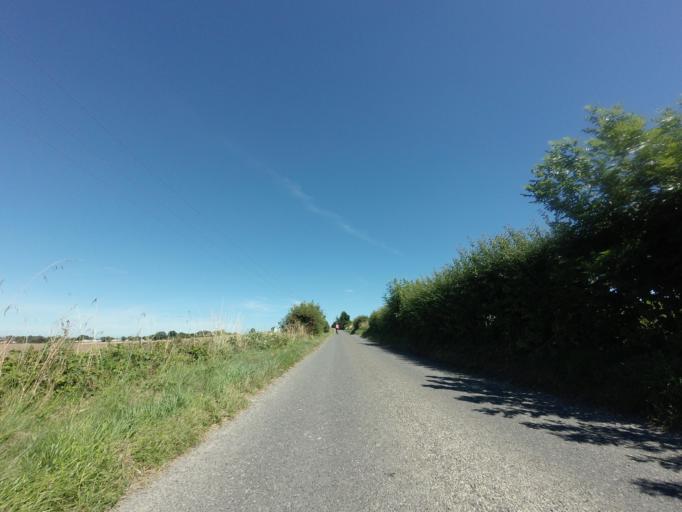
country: GB
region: England
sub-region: Kent
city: Deal
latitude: 51.1939
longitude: 1.3803
